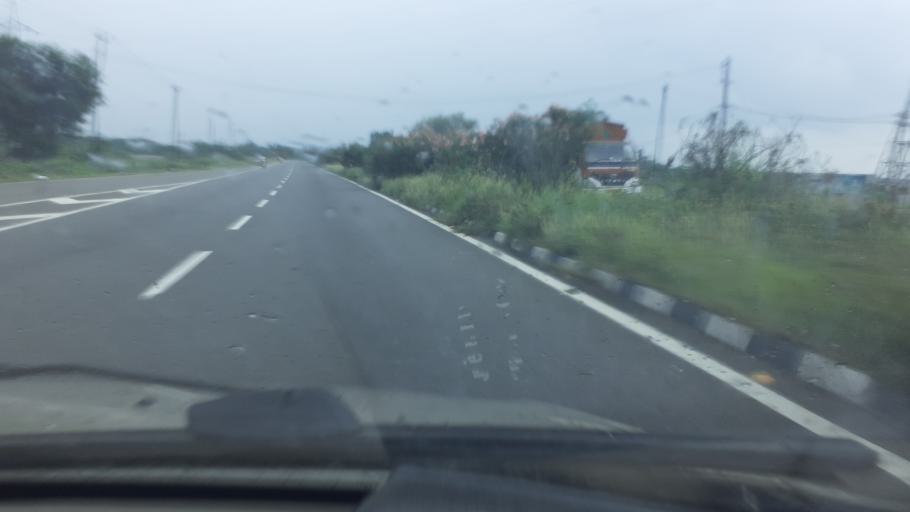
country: IN
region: Tamil Nadu
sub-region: Virudhunagar
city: Virudunagar
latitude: 9.6361
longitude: 77.9610
